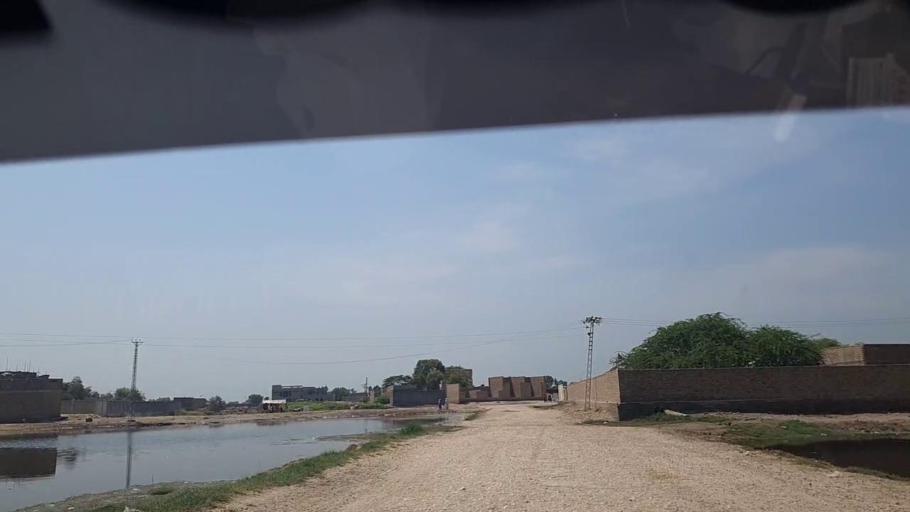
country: PK
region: Sindh
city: Thul
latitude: 28.1780
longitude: 68.7301
